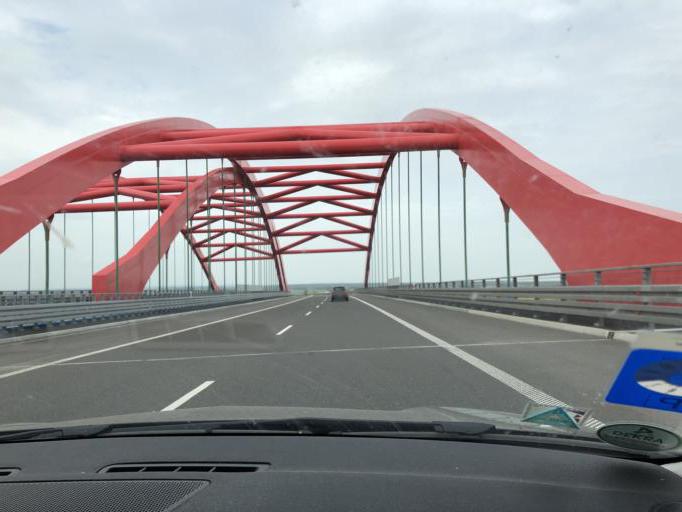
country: PL
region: Subcarpathian Voivodeship
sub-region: Powiat przeworski
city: Rozborz
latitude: 50.0626
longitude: 22.5655
